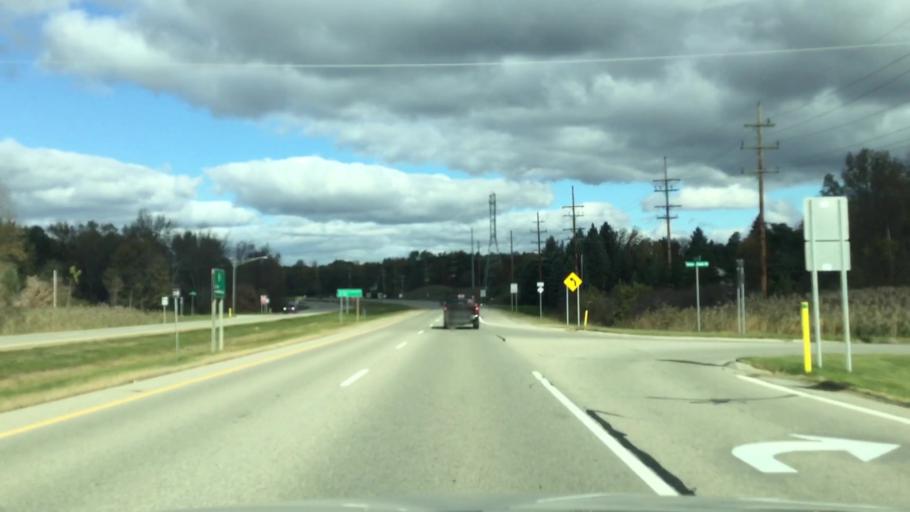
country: US
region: Michigan
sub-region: Lapeer County
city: Lapeer
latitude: 42.9852
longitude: -83.3153
